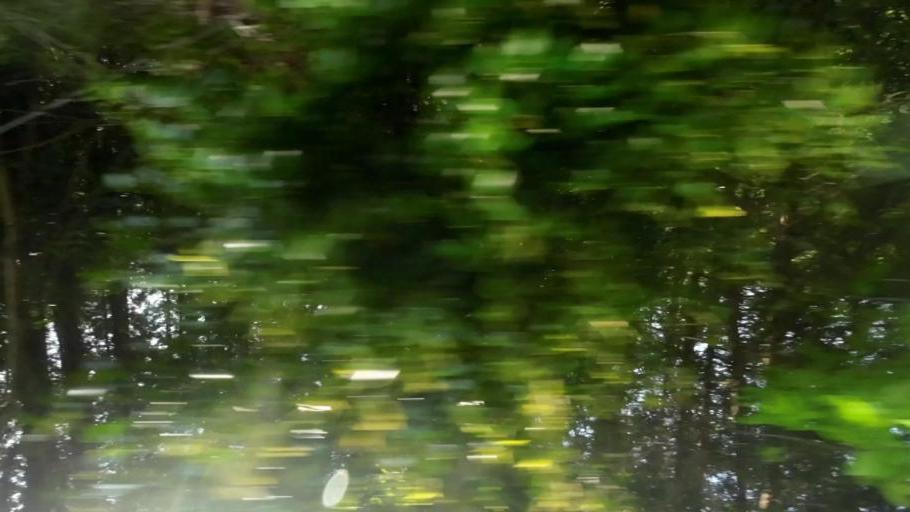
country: JP
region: Ehime
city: Niihama
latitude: 33.9670
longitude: 133.3592
